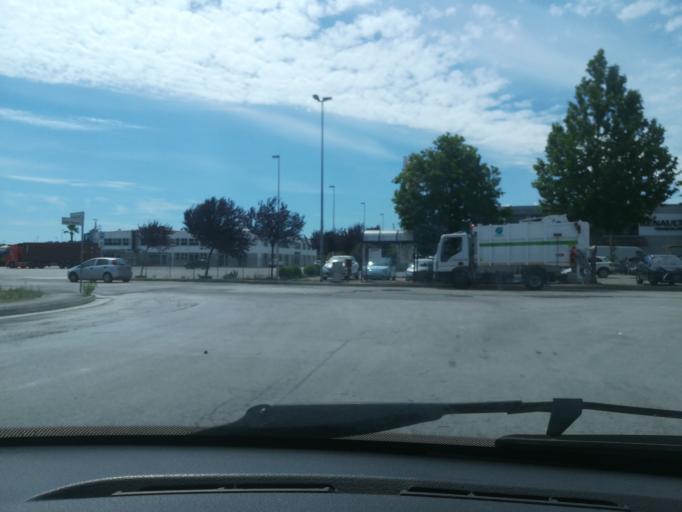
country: IT
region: The Marches
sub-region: Provincia di Macerata
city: Santa Maria Apparente
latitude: 43.2833
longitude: 13.6814
